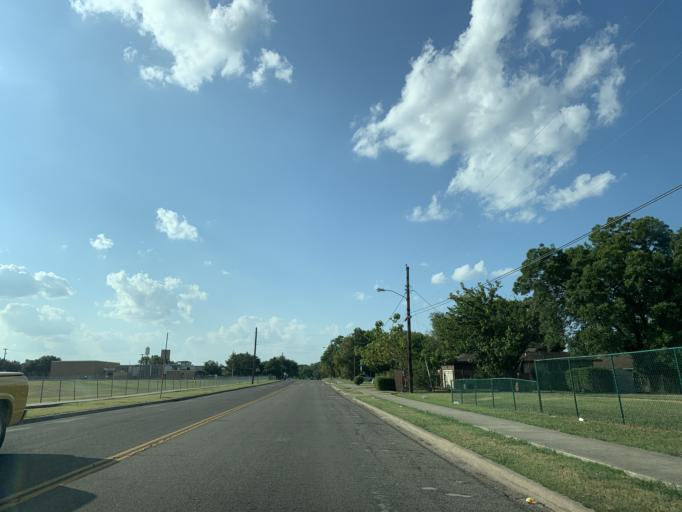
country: US
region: Texas
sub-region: Dallas County
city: Hutchins
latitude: 32.6916
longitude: -96.7810
